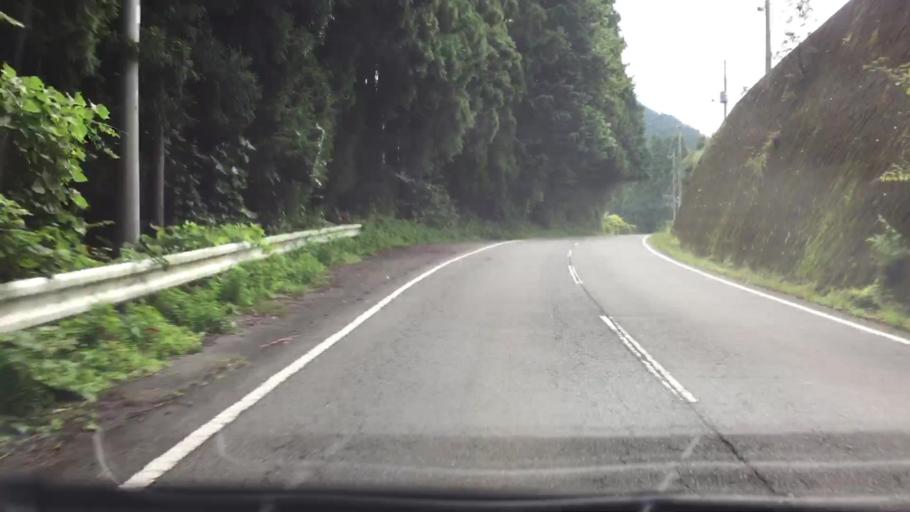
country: JP
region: Tochigi
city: Imaichi
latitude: 36.7608
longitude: 139.6819
